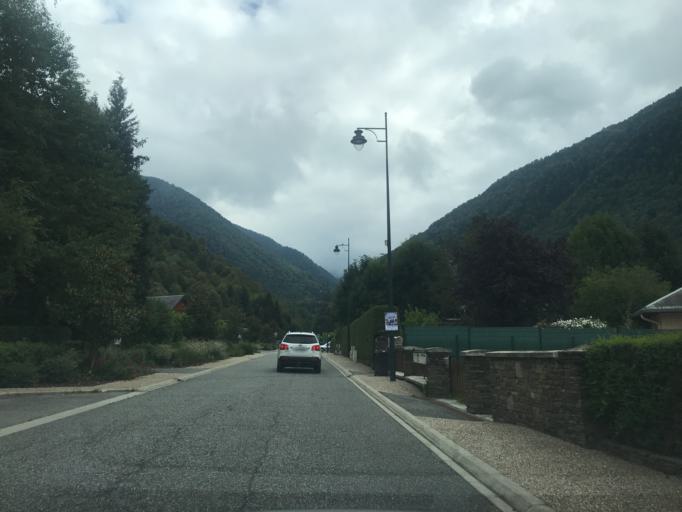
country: FR
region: Midi-Pyrenees
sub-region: Departement de la Haute-Garonne
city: Bagneres-de-Luchon
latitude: 42.7796
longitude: 0.6028
